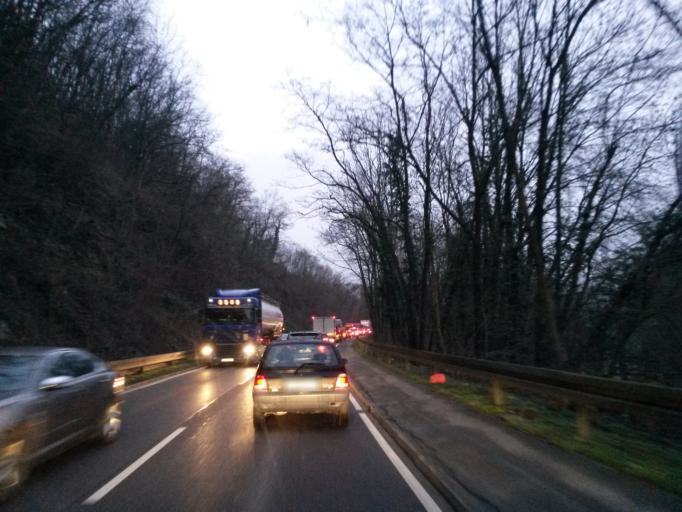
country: DE
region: Baden-Wuerttemberg
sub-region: Regierungsbezirk Stuttgart
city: Benningen am Neckar
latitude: 48.9513
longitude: 9.2503
